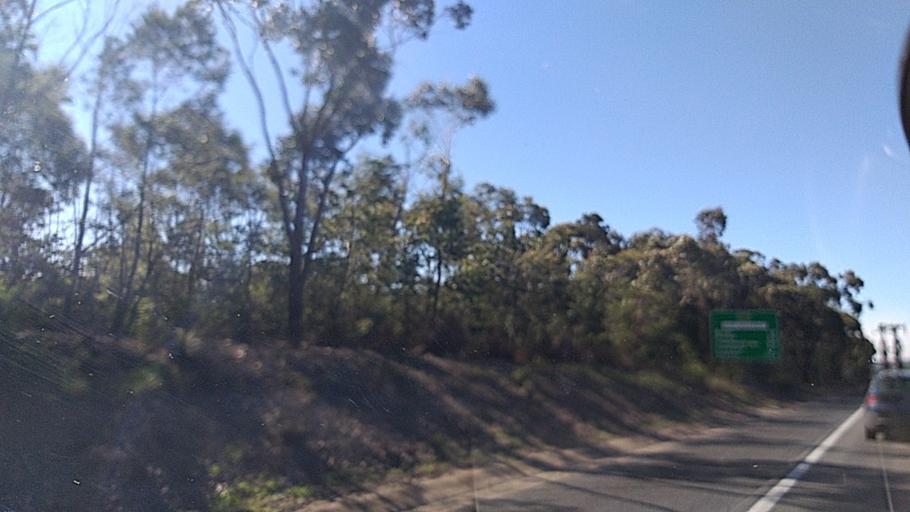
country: AU
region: New South Wales
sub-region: Wingecarribee
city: Colo Vale
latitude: -34.3998
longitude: 150.5110
